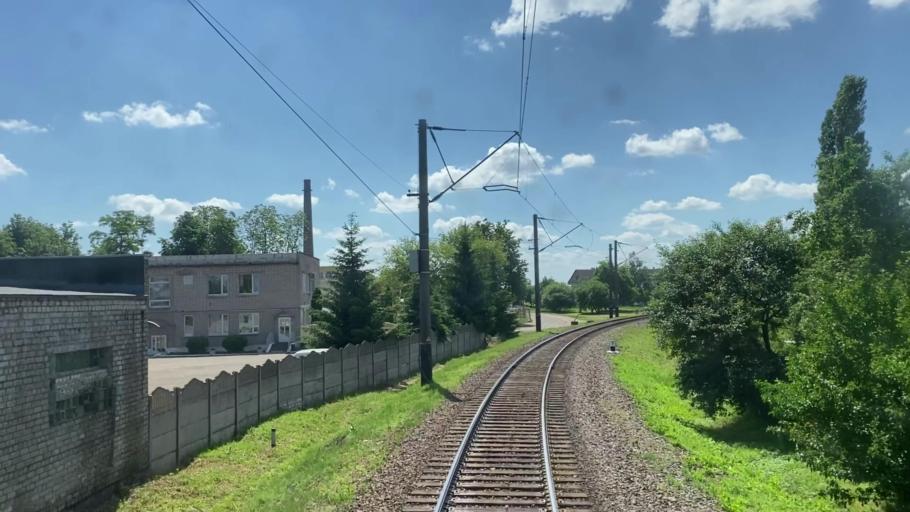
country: BY
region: Brest
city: Baranovichi
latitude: 53.1450
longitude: 26.0325
